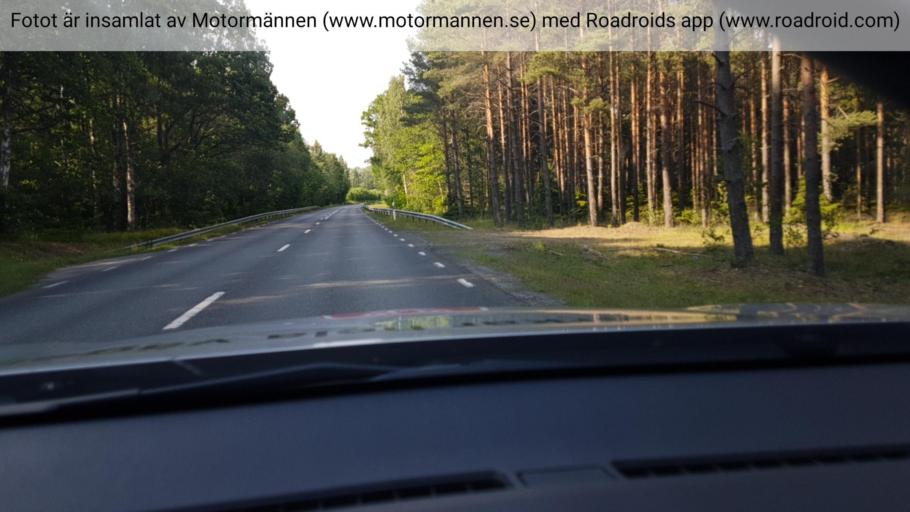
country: SE
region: Vaestra Goetaland
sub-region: Hjo Kommun
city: Hjo
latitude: 58.1084
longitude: 14.2085
